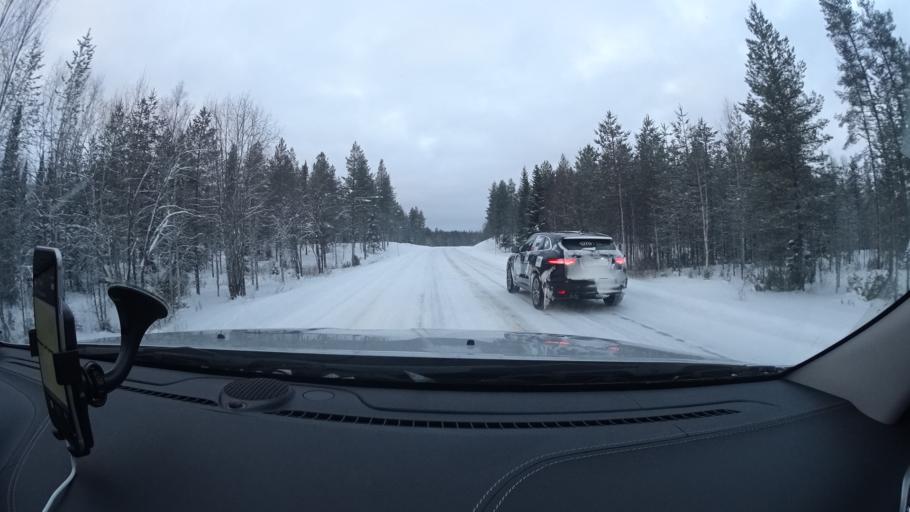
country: FI
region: Lapland
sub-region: Itae-Lappi
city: Posio
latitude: 66.1572
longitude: 28.0507
